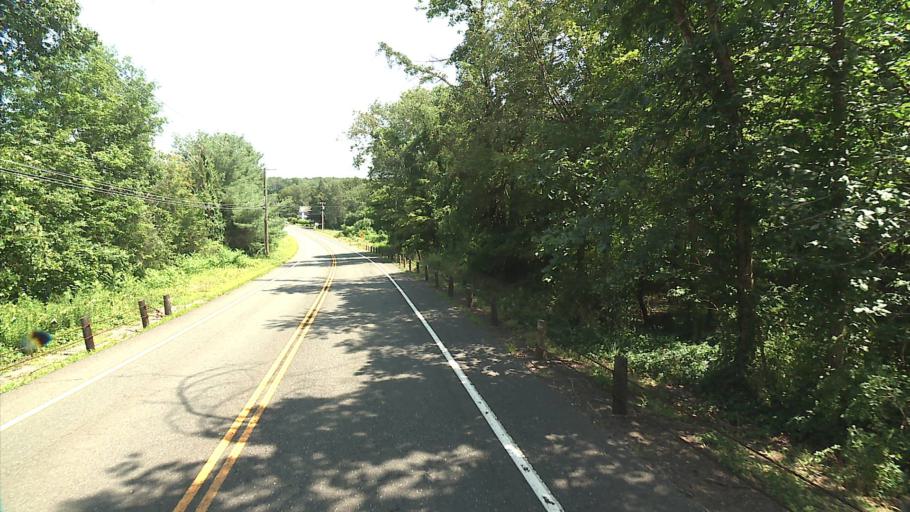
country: US
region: Connecticut
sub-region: Hartford County
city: North Granby
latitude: 41.9571
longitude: -72.8420
